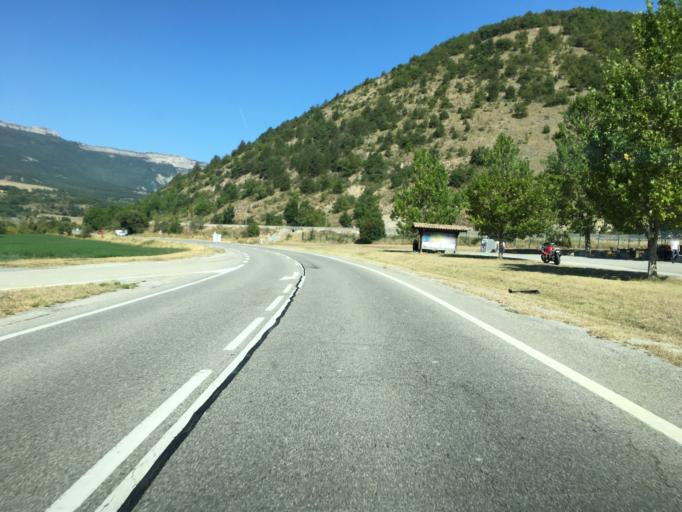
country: FR
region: Provence-Alpes-Cote d'Azur
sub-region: Departement des Hautes-Alpes
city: Serres
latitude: 44.3773
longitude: 5.7485
